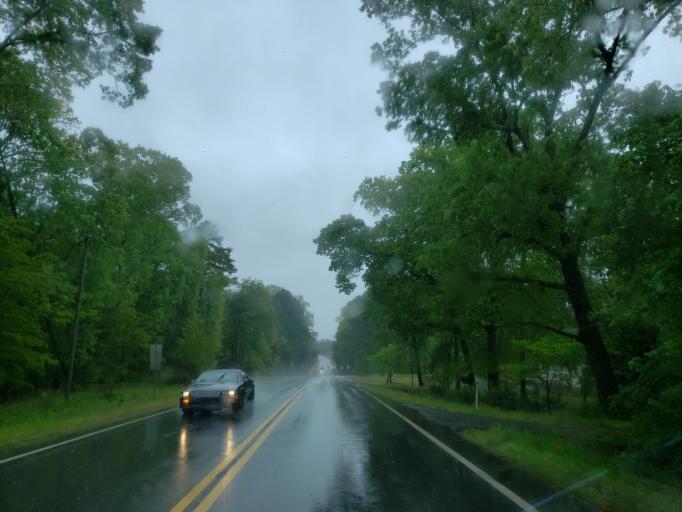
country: US
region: Georgia
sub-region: Carroll County
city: Temple
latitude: 33.7308
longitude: -85.0223
